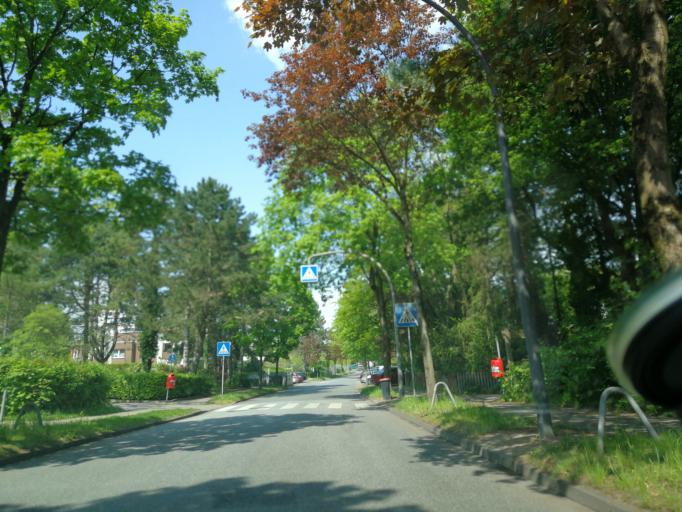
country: DE
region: Schleswig-Holstein
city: Glinde
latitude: 53.5082
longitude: 10.1989
